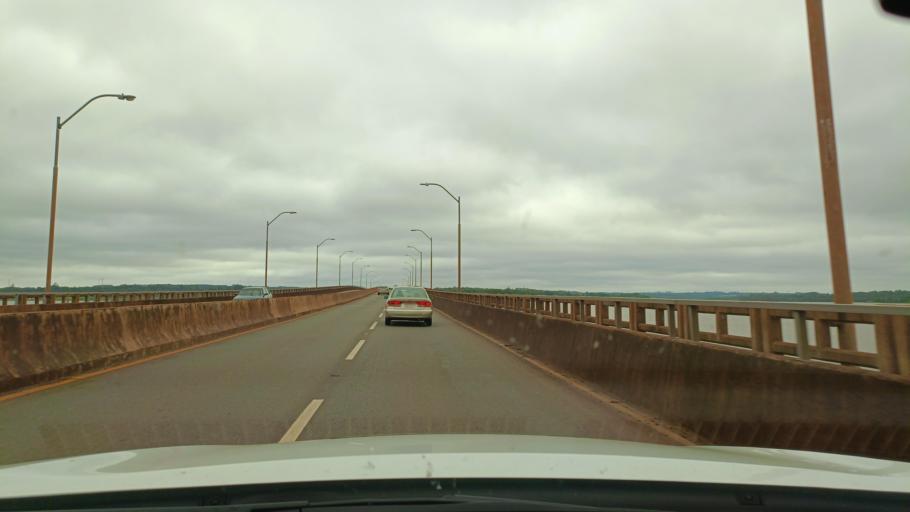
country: PY
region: Itapua
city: Encarnacion
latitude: -27.3005
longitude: -55.9023
